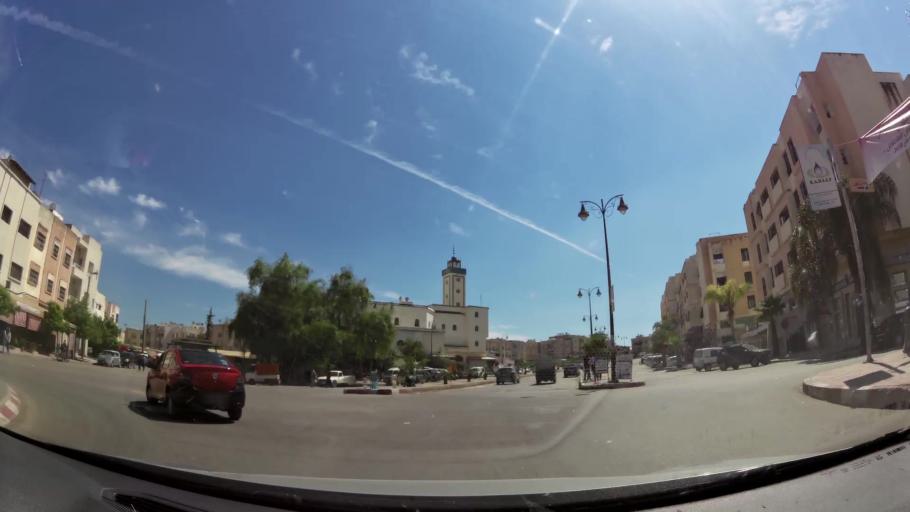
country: MA
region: Fes-Boulemane
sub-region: Fes
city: Fes
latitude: 34.0053
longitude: -4.9848
